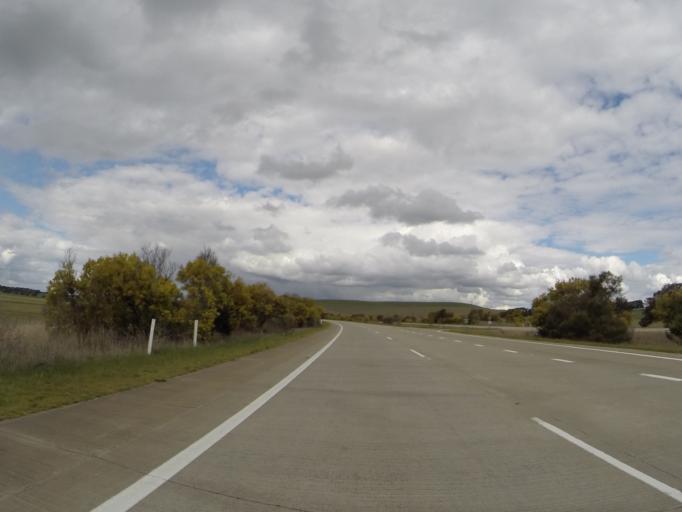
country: AU
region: New South Wales
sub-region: Goulburn Mulwaree
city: Goulburn
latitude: -34.8062
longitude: 149.5159
